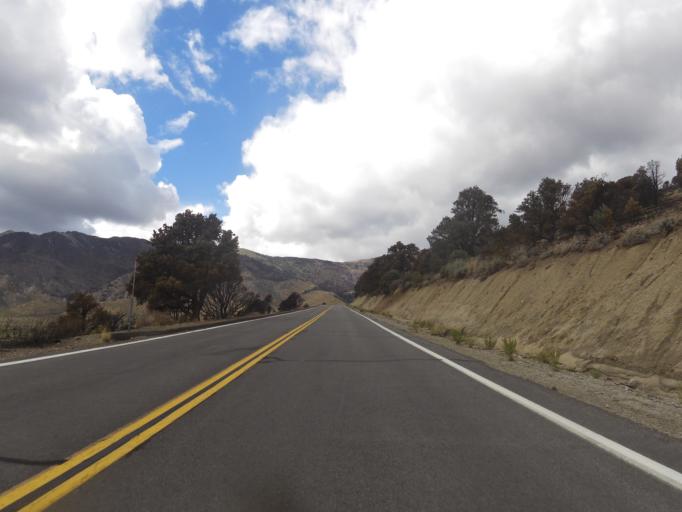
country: US
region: Nevada
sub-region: Lyon County
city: Smith Valley
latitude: 38.6473
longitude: -119.5637
